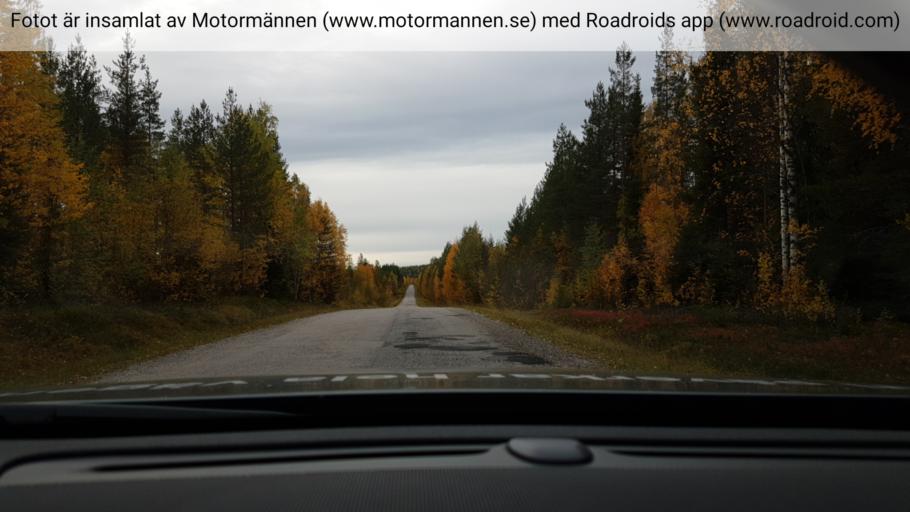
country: SE
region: Norrbotten
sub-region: Overkalix Kommun
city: OEverkalix
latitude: 66.2584
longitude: 23.0234
